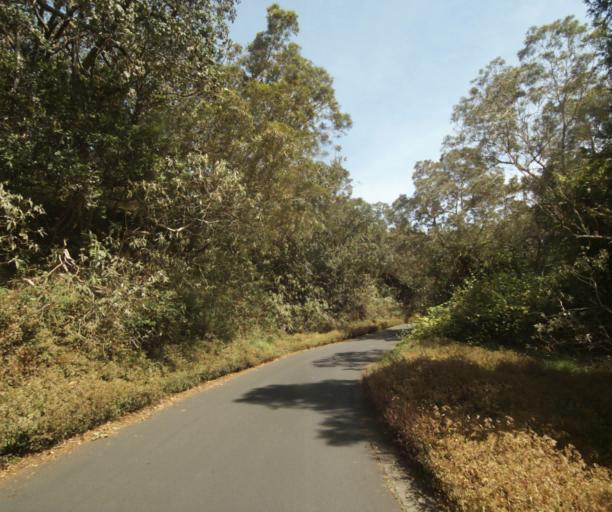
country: RE
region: Reunion
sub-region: Reunion
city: Trois-Bassins
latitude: -21.0556
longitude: 55.3608
